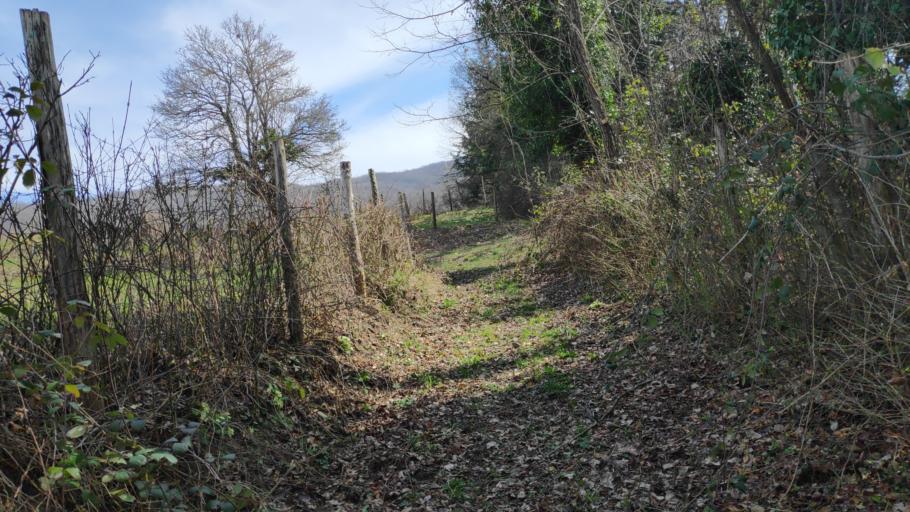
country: IT
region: Emilia-Romagna
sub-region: Provincia di Bologna
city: Berzantina
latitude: 44.1747
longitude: 10.9917
